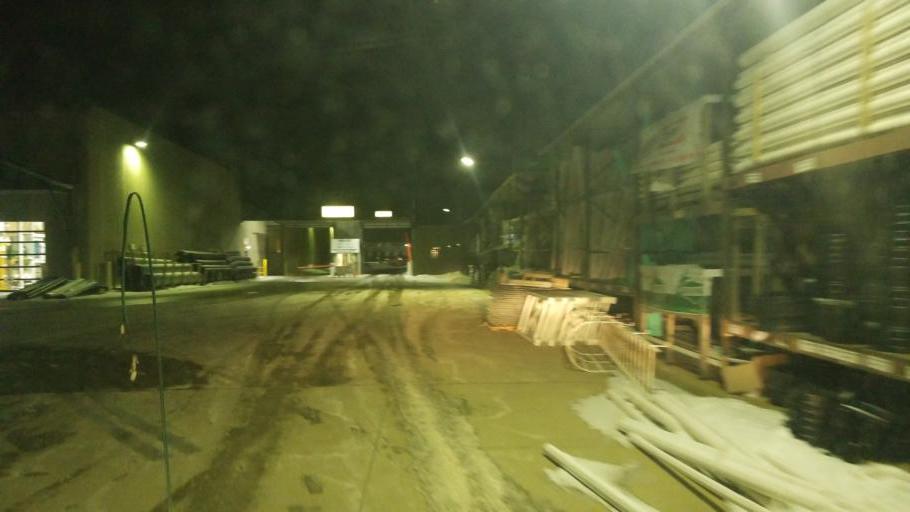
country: US
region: Ohio
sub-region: Richland County
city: Ontario
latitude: 40.7871
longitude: -82.5838
